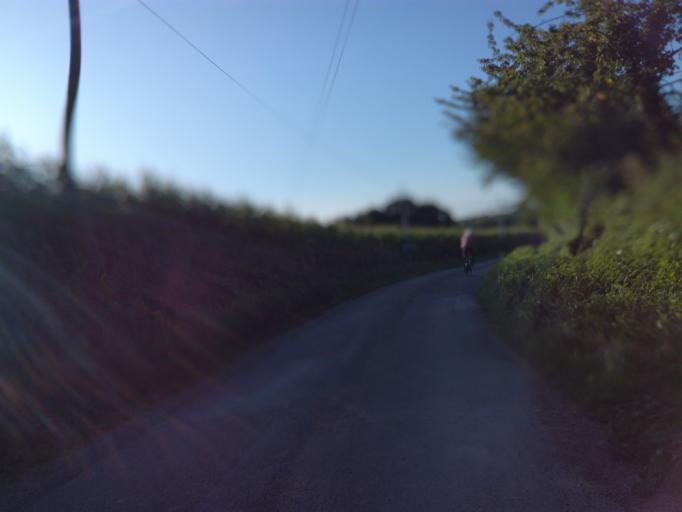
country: FR
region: Brittany
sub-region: Departement d'Ille-et-Vilaine
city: Betton
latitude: 48.1678
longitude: -1.6355
